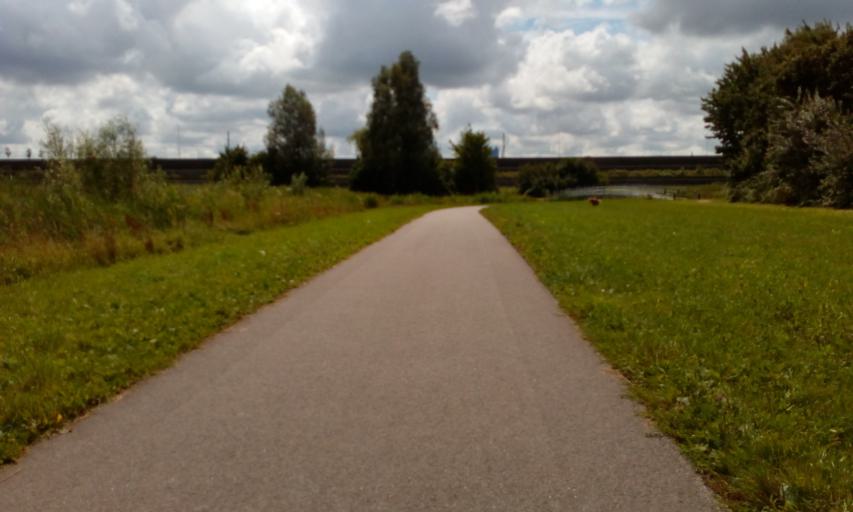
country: NL
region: South Holland
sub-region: Gemeente Binnenmaas
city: Heinenoord
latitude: 51.8655
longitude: 4.4880
